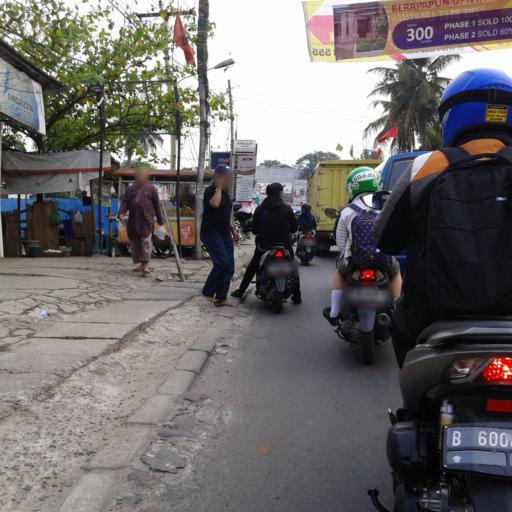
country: ID
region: West Java
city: Sawangan
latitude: -6.4021
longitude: 106.7712
